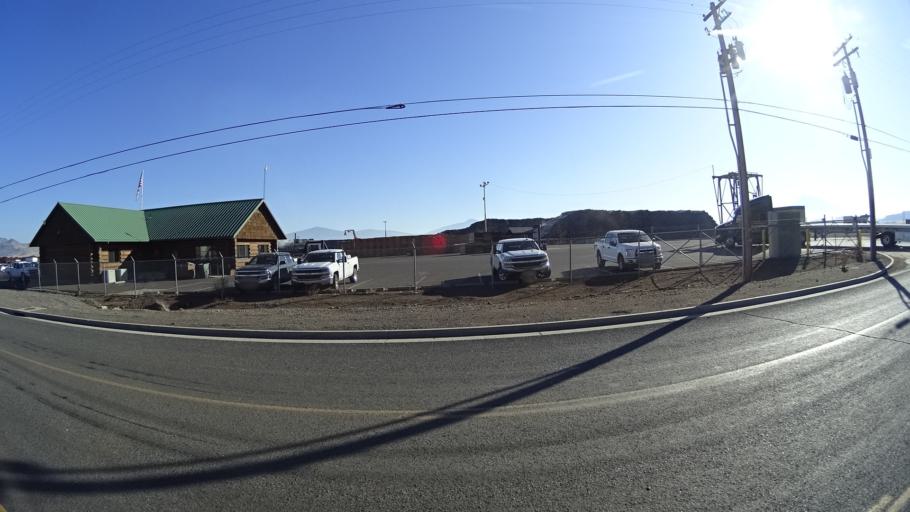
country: US
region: California
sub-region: Siskiyou County
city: Yreka
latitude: 41.7306
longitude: -122.5933
